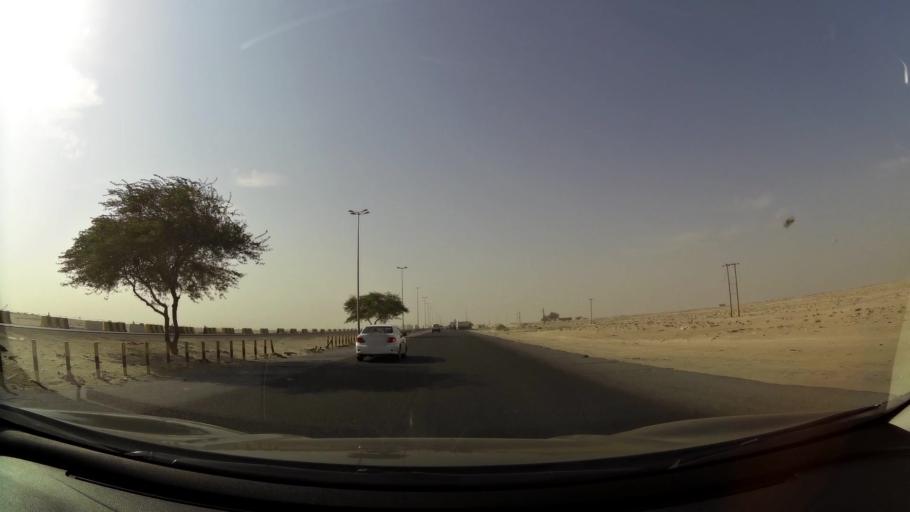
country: KW
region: Al Ahmadi
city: Al Ahmadi
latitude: 28.9170
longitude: 48.0996
